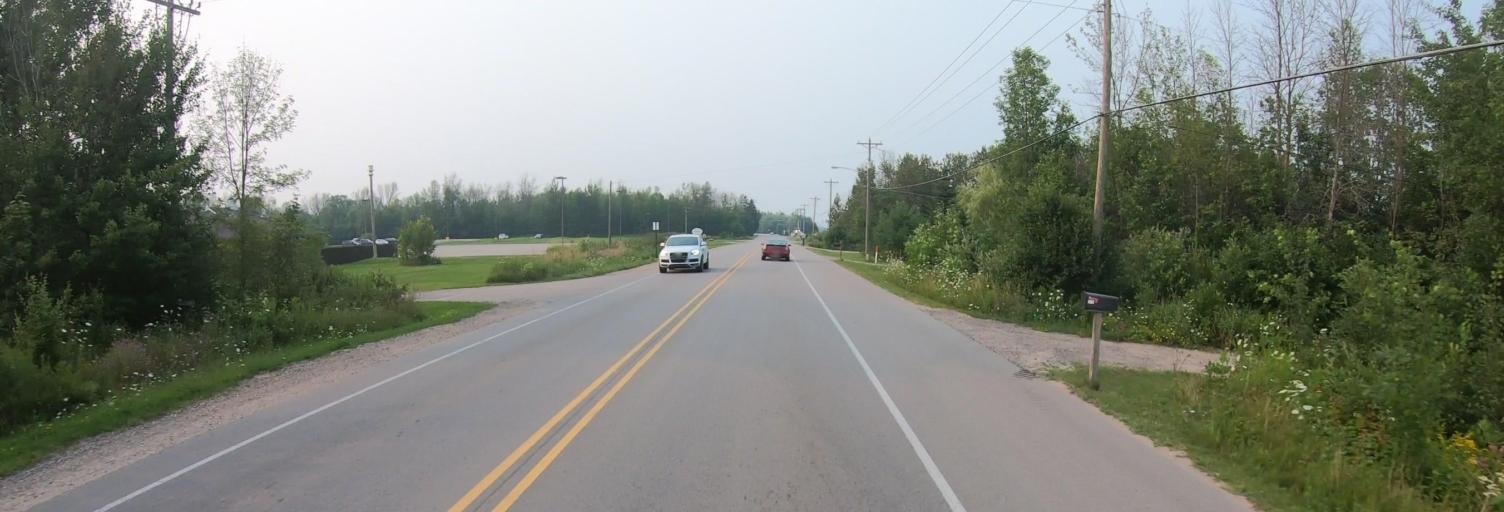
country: US
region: Michigan
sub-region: Chippewa County
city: Sault Ste. Marie
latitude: 46.4193
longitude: -84.6037
